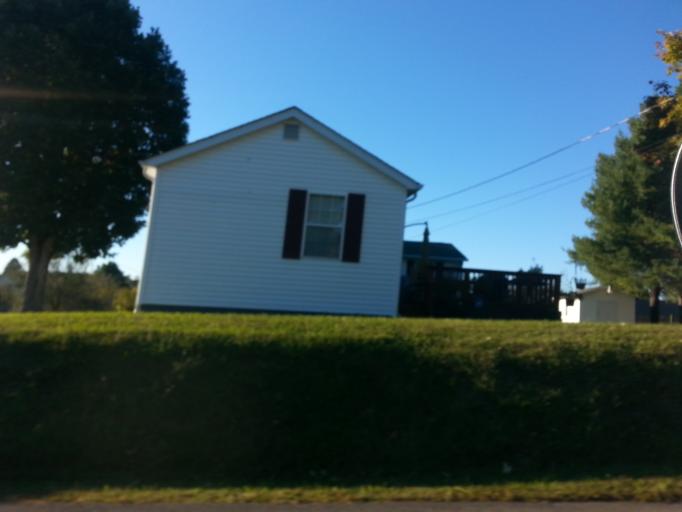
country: US
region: Tennessee
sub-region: Blount County
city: Eagleton Village
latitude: 35.7752
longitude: -83.9280
